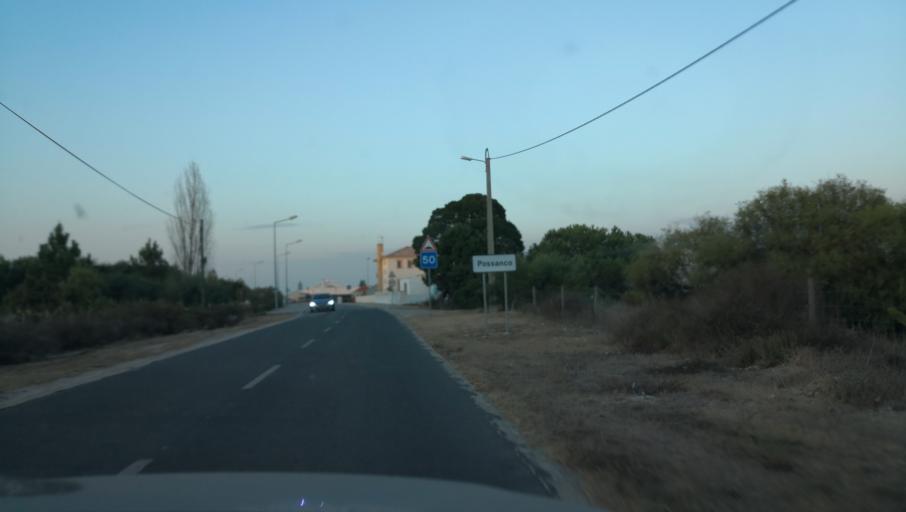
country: PT
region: Setubal
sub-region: Setubal
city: Setubal
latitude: 38.3931
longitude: -8.7787
